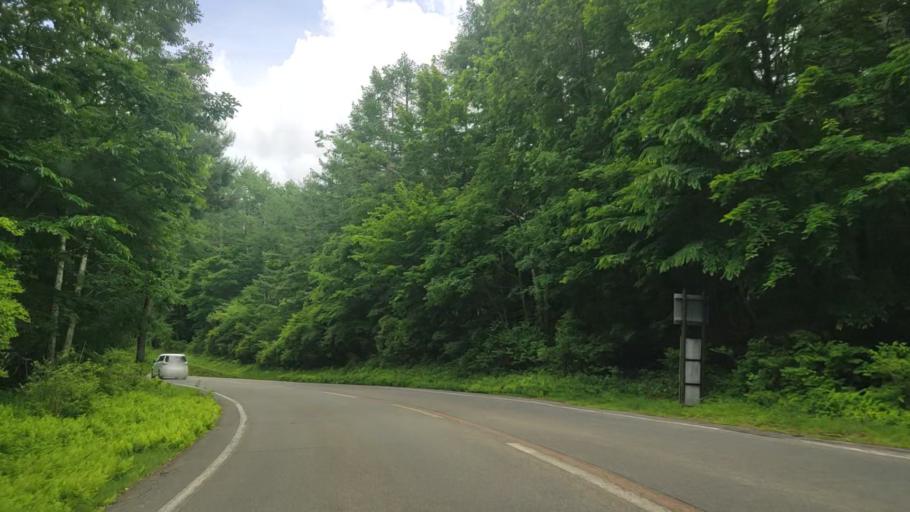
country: JP
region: Yamanashi
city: Fujikawaguchiko
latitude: 35.4233
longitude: 138.7349
